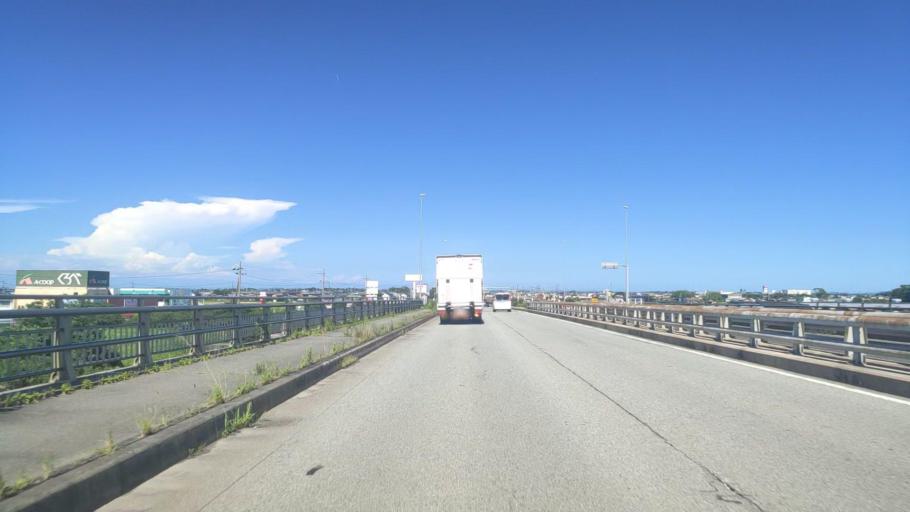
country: JP
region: Mie
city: Hisai-motomachi
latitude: 34.5863
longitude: 136.5863
